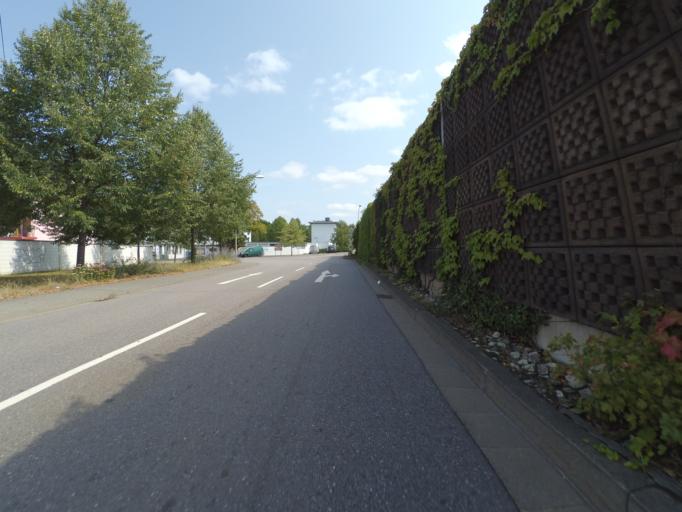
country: DE
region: Saarland
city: Merzig
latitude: 49.4424
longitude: 6.6422
